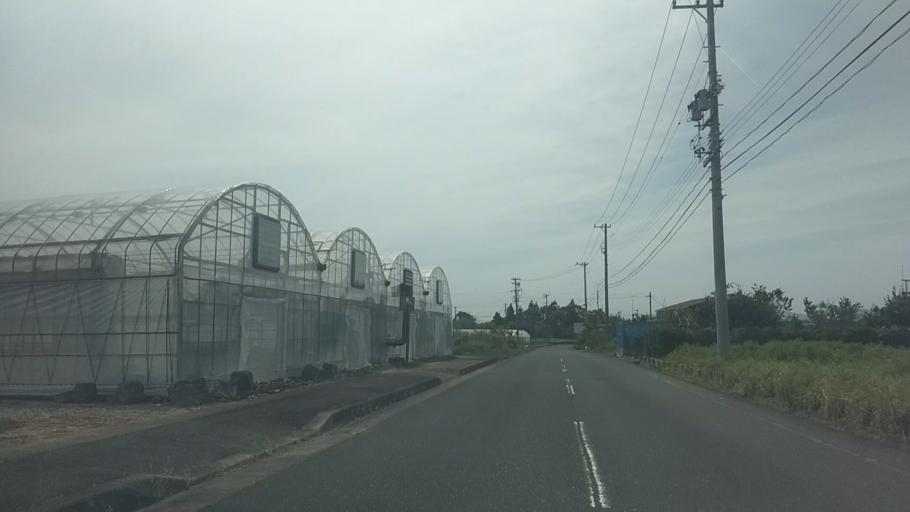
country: JP
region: Shizuoka
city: Kosai-shi
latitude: 34.7788
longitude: 137.6375
